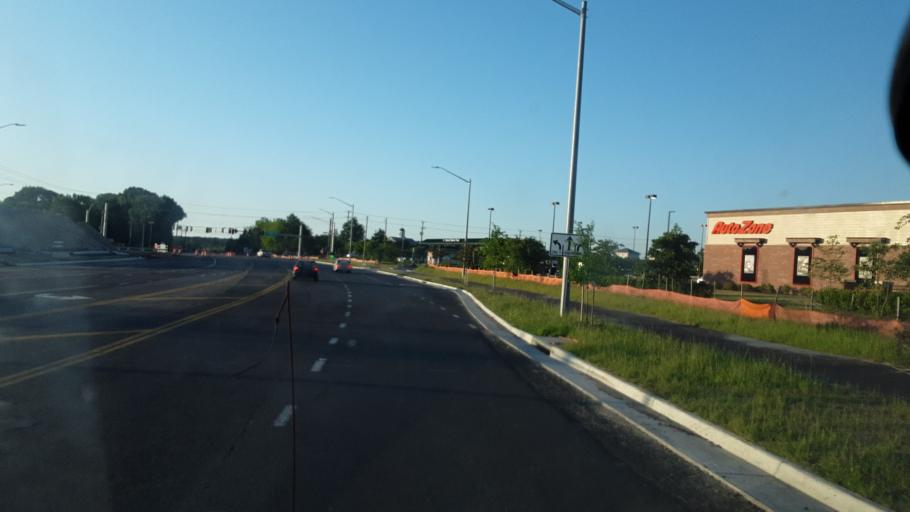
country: US
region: Virginia
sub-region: City of Virginia Beach
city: Virginia Beach
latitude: 36.7533
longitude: -76.0113
